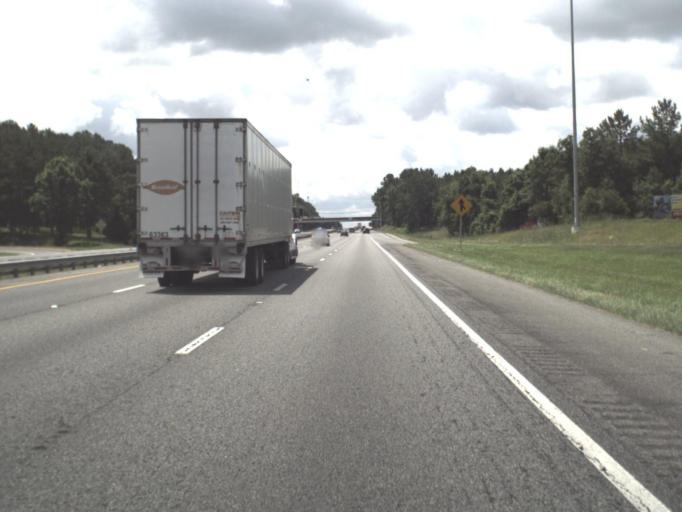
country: US
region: Florida
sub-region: Suwannee County
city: Wellborn
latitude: 30.2657
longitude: -82.7540
